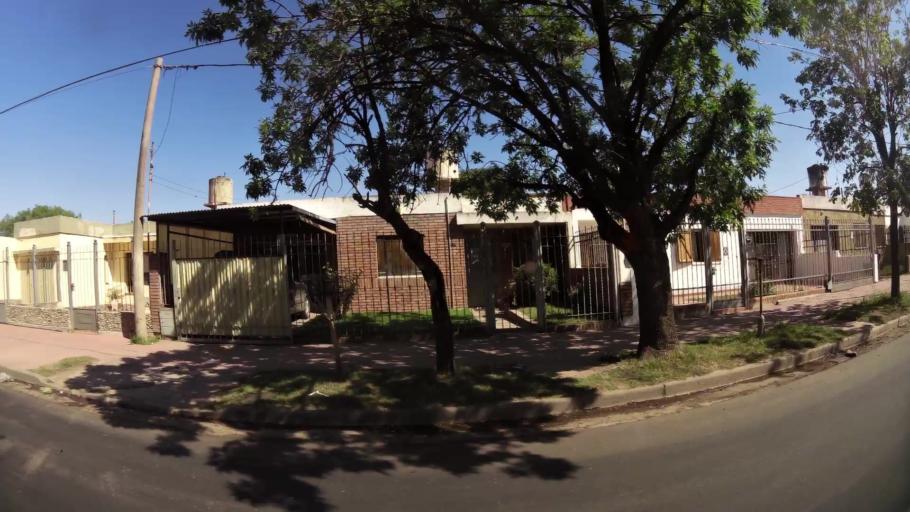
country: AR
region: Cordoba
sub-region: Departamento de Capital
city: Cordoba
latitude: -31.3709
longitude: -64.1664
